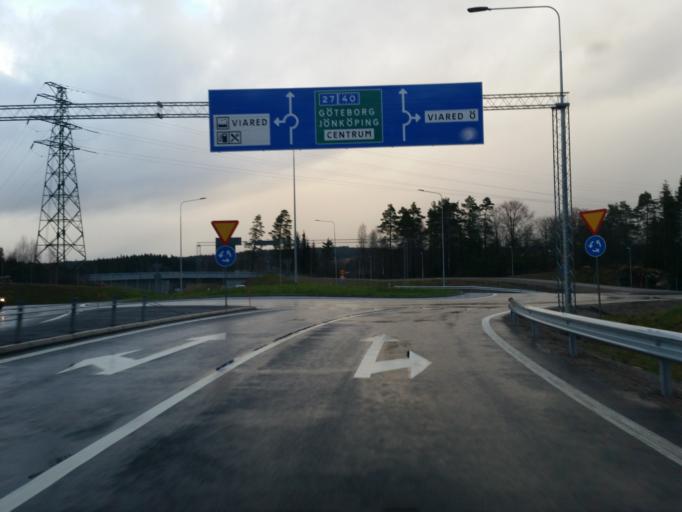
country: SE
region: Vaestra Goetaland
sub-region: Boras Kommun
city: Sjomarken
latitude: 57.7077
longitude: 12.8721
